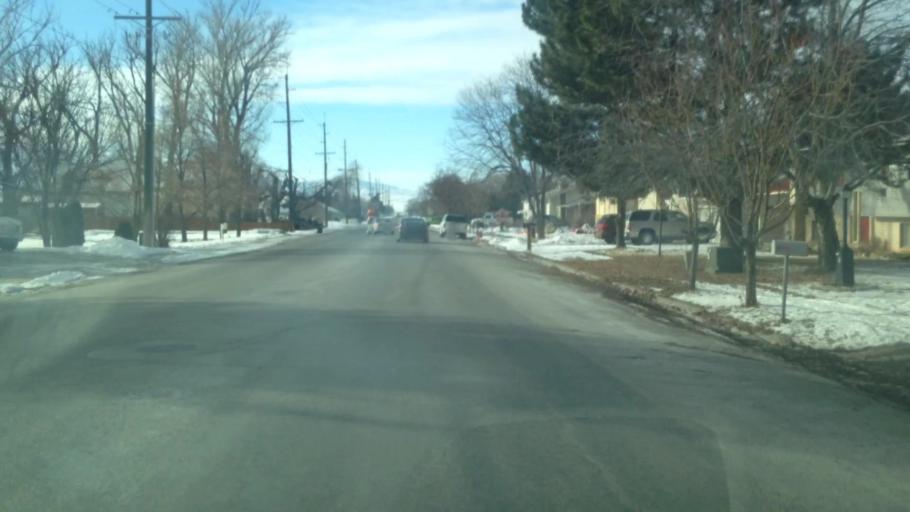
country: US
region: Utah
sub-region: Cache County
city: Logan
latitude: 41.7503
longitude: -111.8413
